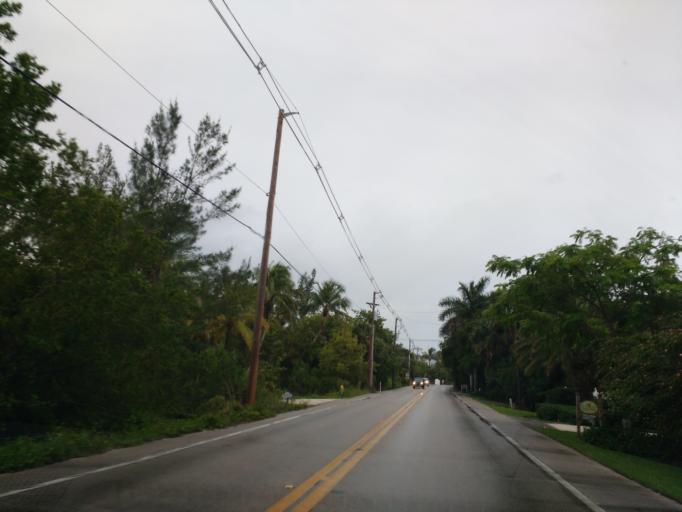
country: US
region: Florida
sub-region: Lee County
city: Saint James City
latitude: 26.4863
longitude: -82.1837
